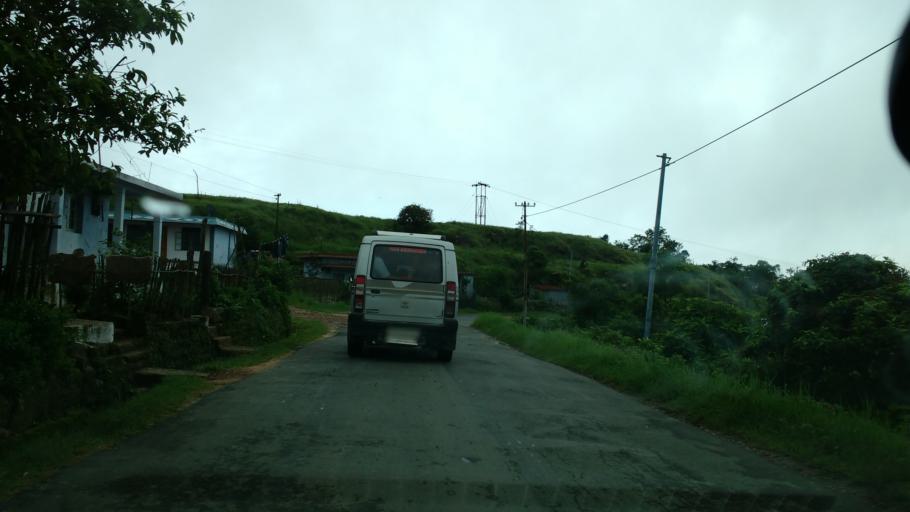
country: IN
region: Meghalaya
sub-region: East Khasi Hills
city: Cherrapunji
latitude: 25.2429
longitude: 91.7317
